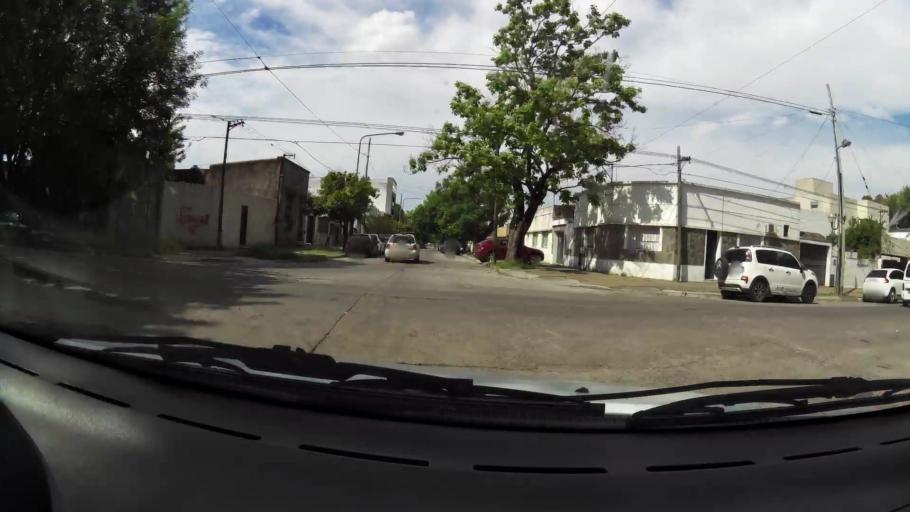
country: AR
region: Buenos Aires
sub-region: Partido de La Plata
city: La Plata
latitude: -34.9227
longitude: -57.9209
